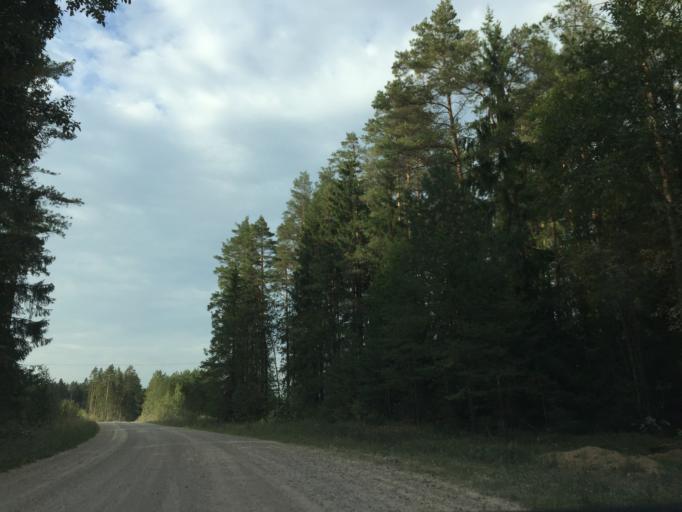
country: LV
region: Baldone
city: Baldone
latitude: 56.7885
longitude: 24.4431
